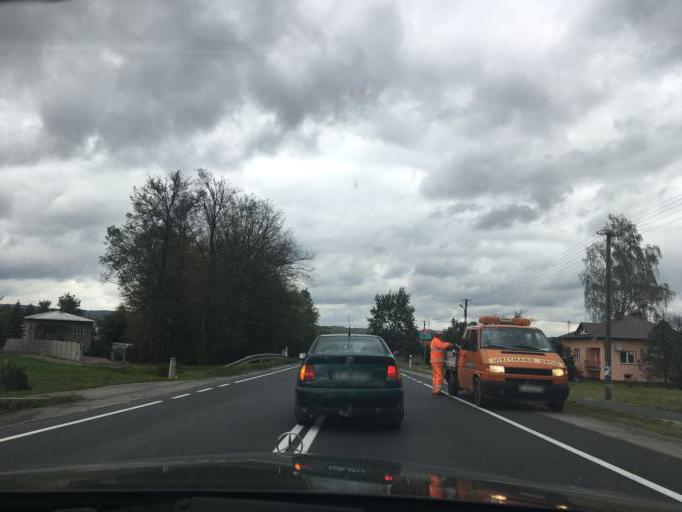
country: PL
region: Subcarpathian Voivodeship
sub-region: Powiat krosnienski
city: Kroscienko Wyzne
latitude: 49.6711
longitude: 21.8470
